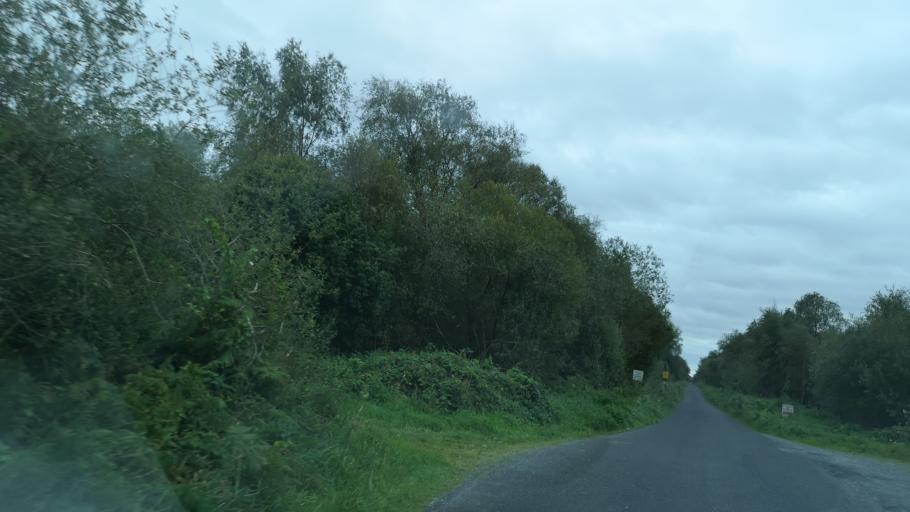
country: IE
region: Leinster
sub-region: Uibh Fhaili
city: Ferbane
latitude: 53.1997
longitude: -7.7251
